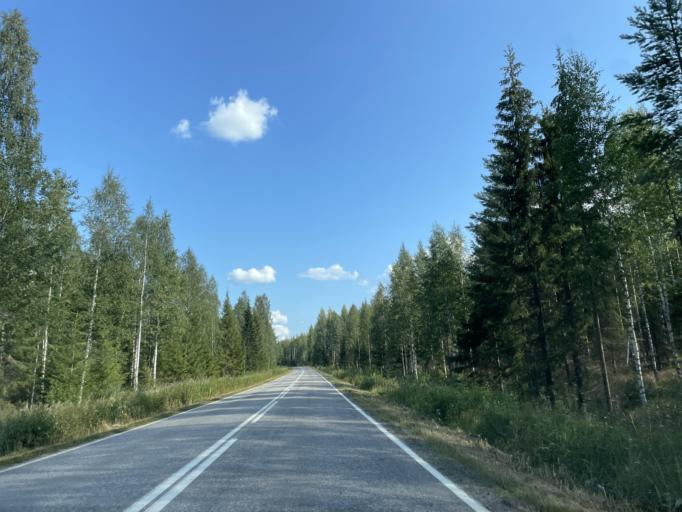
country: FI
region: Central Finland
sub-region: Saarijaervi-Viitasaari
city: Pihtipudas
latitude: 63.3672
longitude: 25.6901
